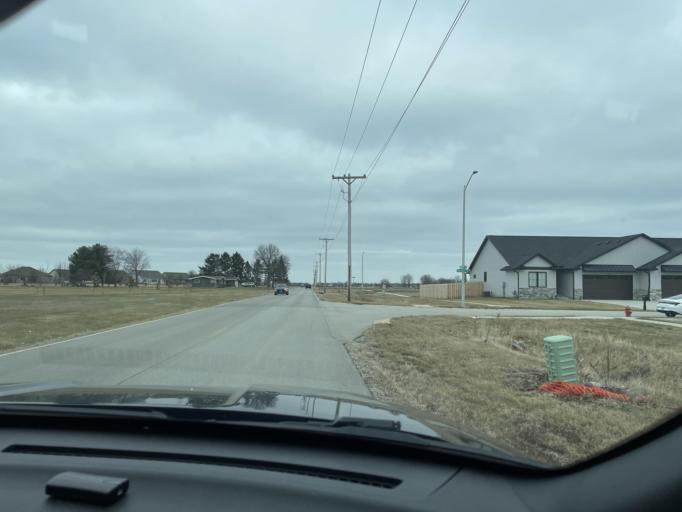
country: US
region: Illinois
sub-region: Sangamon County
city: Jerome
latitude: 39.7620
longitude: -89.7532
